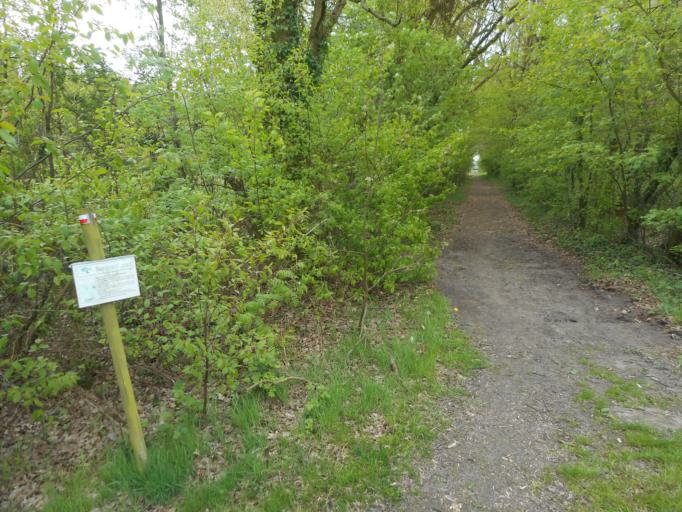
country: BE
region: Flanders
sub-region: Provincie Antwerpen
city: Sint-Katelijne-Waver
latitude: 51.0802
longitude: 4.5674
